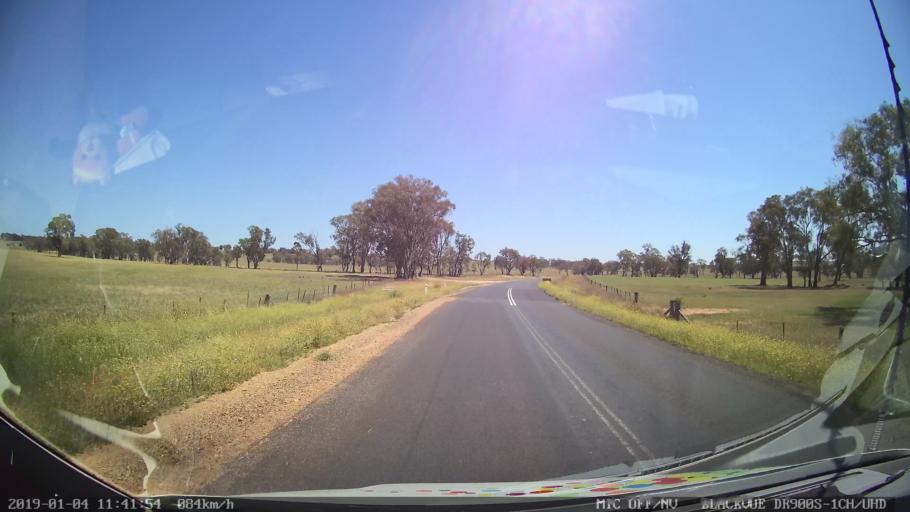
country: AU
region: New South Wales
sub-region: Cabonne
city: Molong
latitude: -32.9884
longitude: 148.7868
